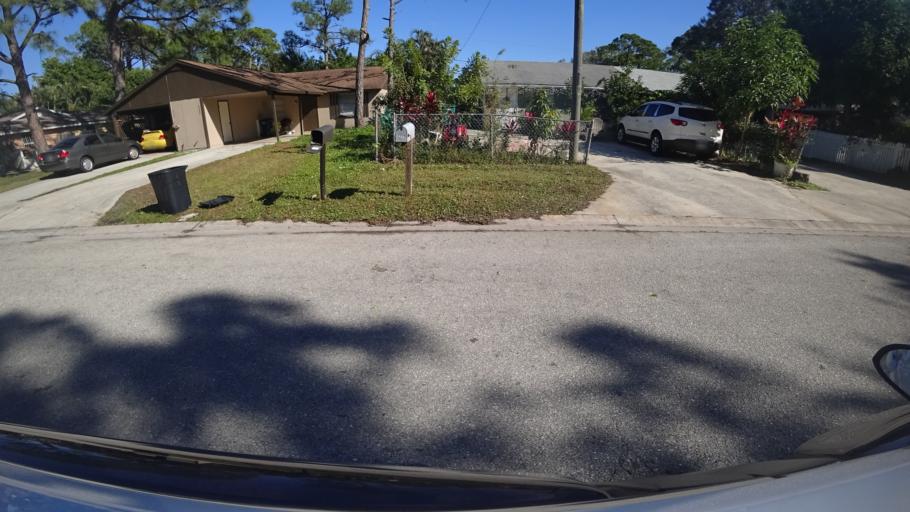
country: US
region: Florida
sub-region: Manatee County
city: Whitfield
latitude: 27.4301
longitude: -82.5525
